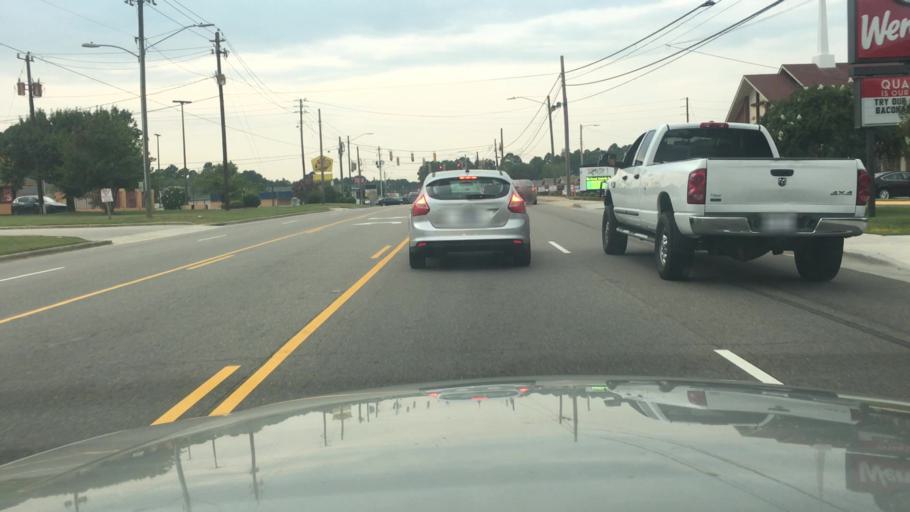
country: US
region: North Carolina
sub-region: Cumberland County
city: Fort Bragg
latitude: 35.0909
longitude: -78.9835
